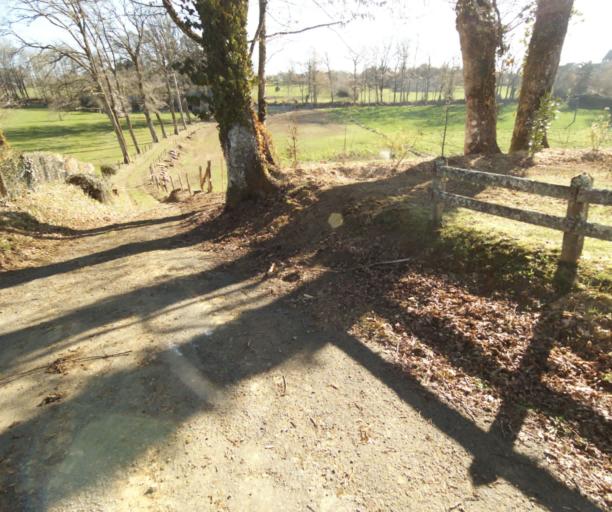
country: FR
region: Limousin
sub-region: Departement de la Correze
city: Seilhac
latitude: 45.3940
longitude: 1.7621
